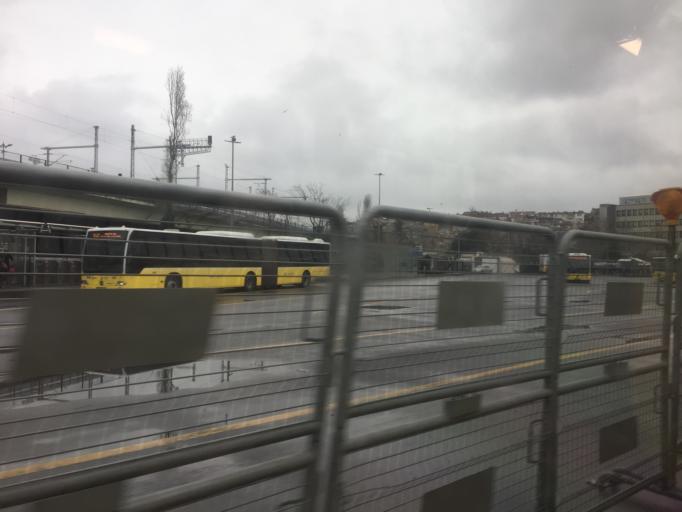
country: TR
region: Istanbul
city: UEskuedar
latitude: 40.9914
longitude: 29.0380
